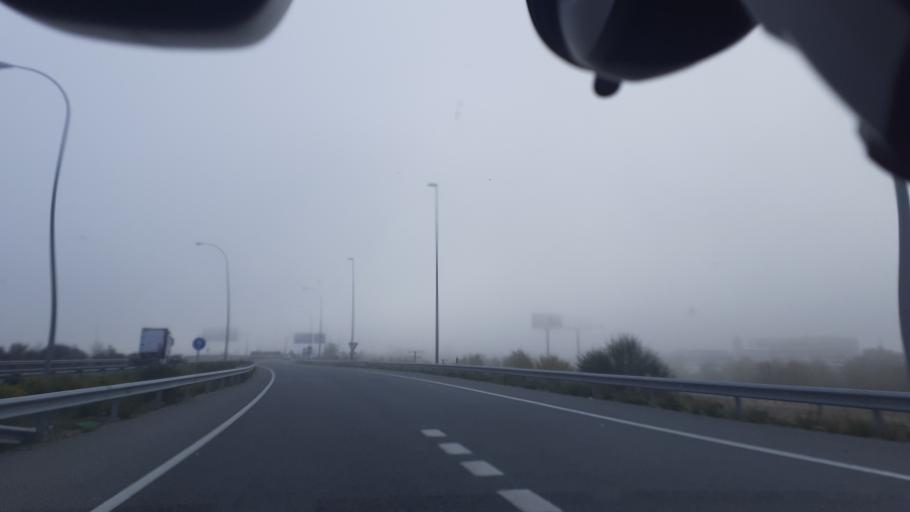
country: ES
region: Madrid
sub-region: Provincia de Madrid
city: Vicalvaro
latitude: 40.3970
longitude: -3.5765
